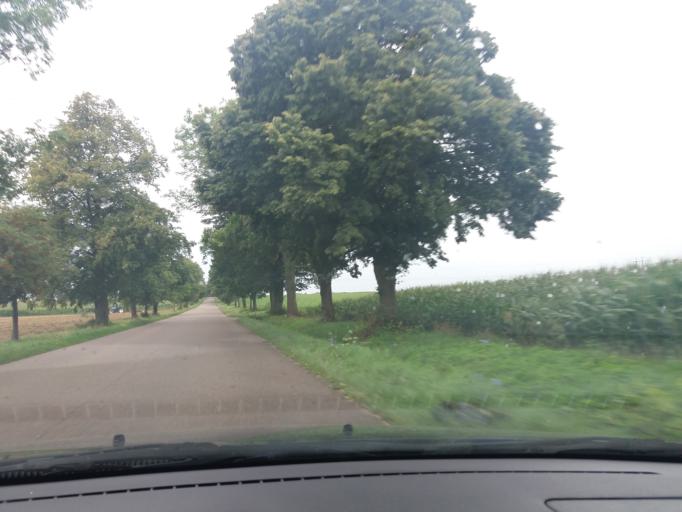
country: PL
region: Masovian Voivodeship
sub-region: Powiat mlawski
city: Wieczfnia Koscielna
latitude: 53.1911
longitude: 20.4625
